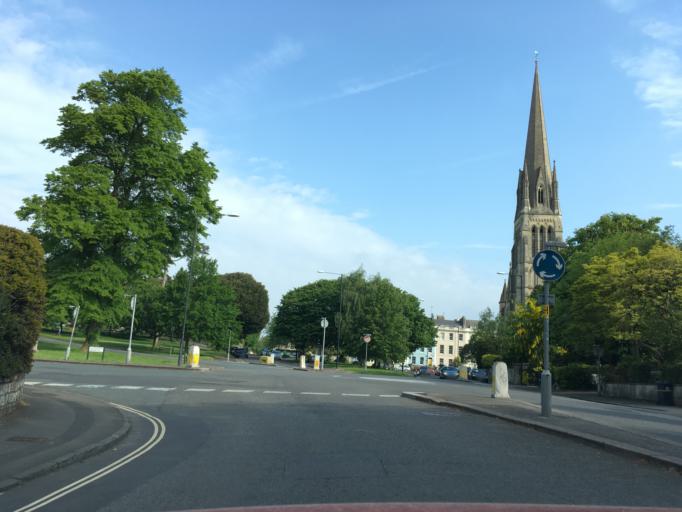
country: GB
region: England
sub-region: Bristol
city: Bristol
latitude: 51.4565
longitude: -2.6200
